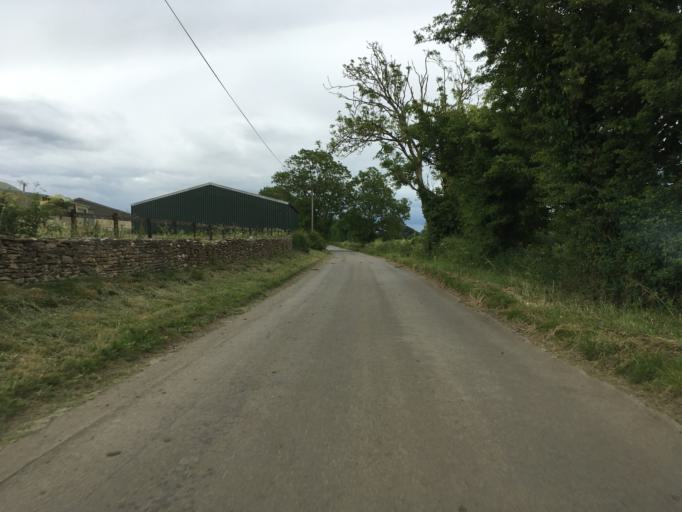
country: GB
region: England
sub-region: Wiltshire
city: Luckington
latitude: 51.5727
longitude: -2.2280
